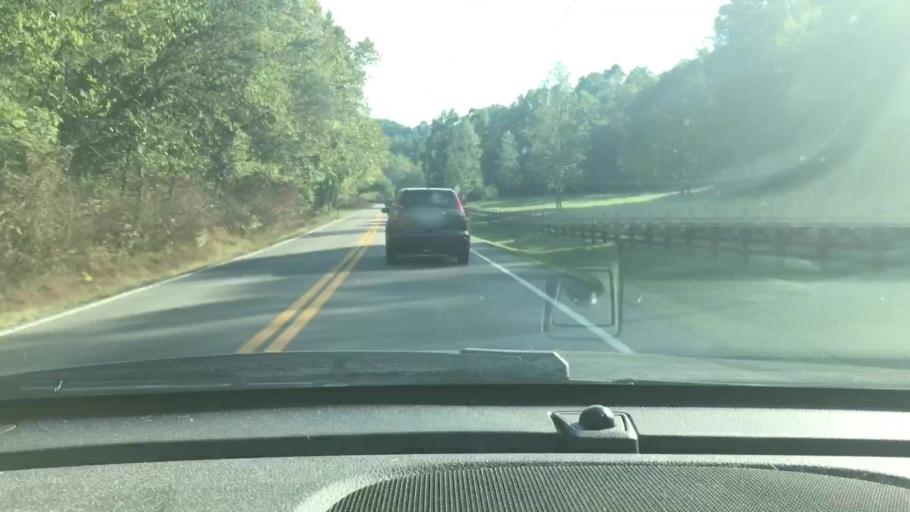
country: US
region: Tennessee
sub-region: Sumner County
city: White House
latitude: 36.4296
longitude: -86.6584
